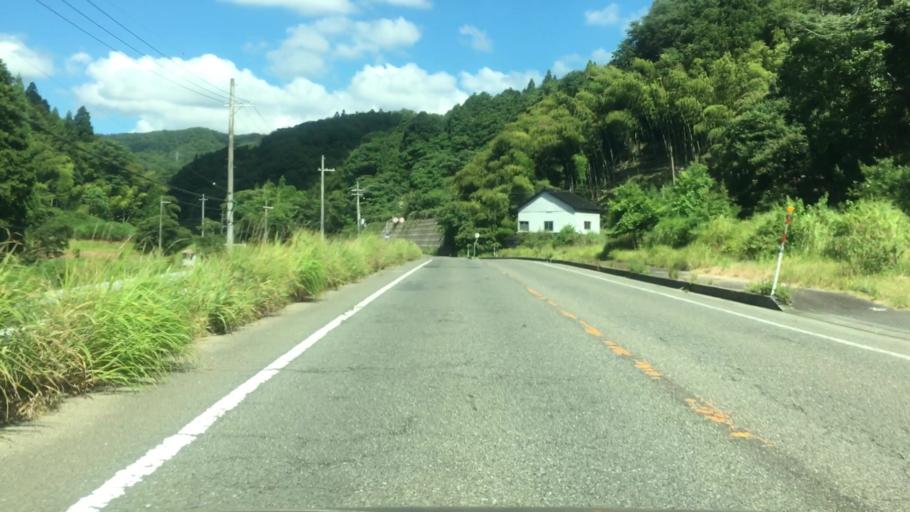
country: JP
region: Hyogo
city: Toyooka
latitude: 35.5752
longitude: 134.7641
